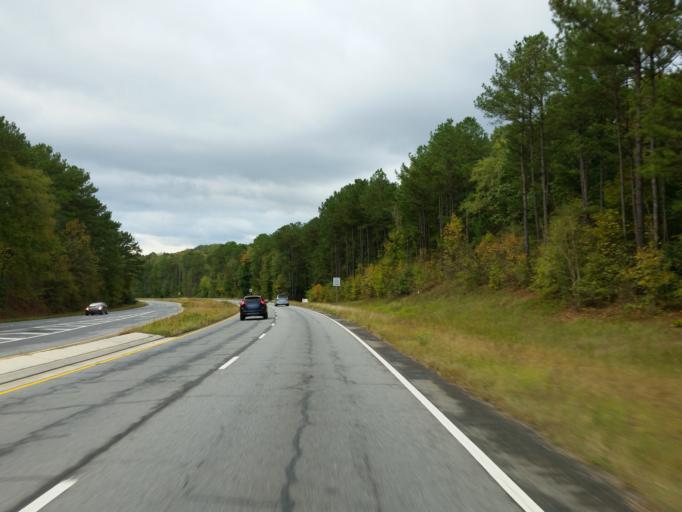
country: US
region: Georgia
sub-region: Bartow County
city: Emerson
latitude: 34.0818
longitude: -84.7306
